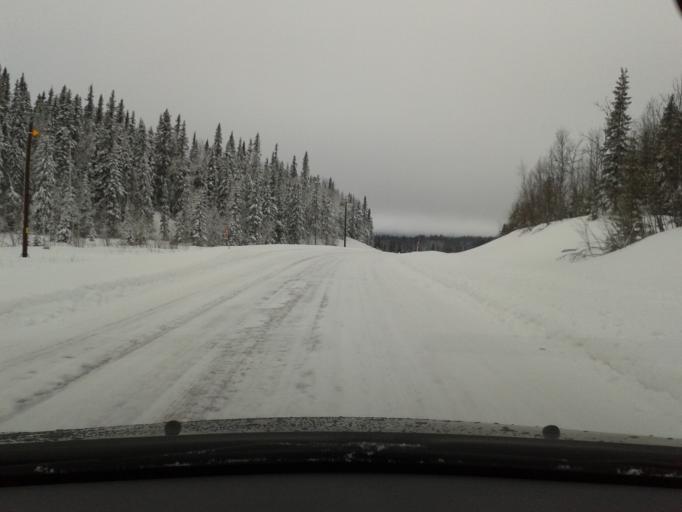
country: SE
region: Vaesterbotten
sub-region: Vilhelmina Kommun
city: Sjoberg
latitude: 65.1829
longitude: 15.9122
